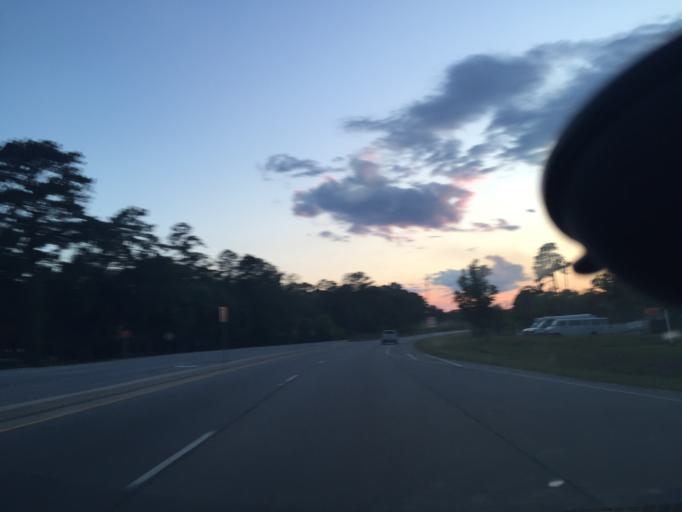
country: US
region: Georgia
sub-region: Chatham County
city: Wilmington Island
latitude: 32.0319
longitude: -80.9646
